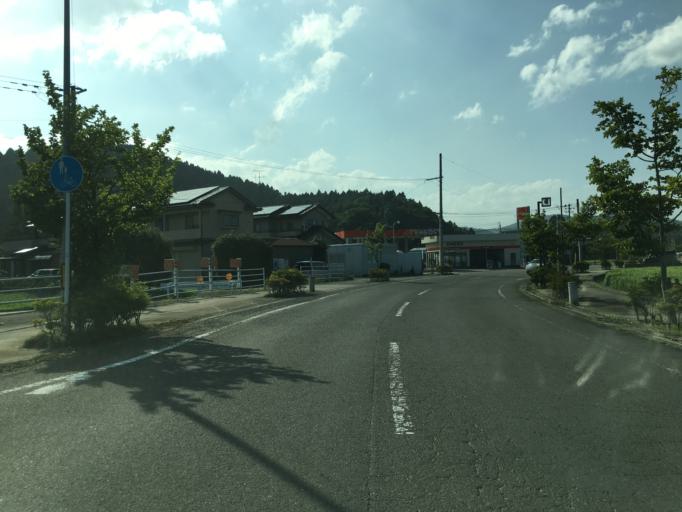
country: JP
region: Miyagi
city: Marumori
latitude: 37.9261
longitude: 140.7655
